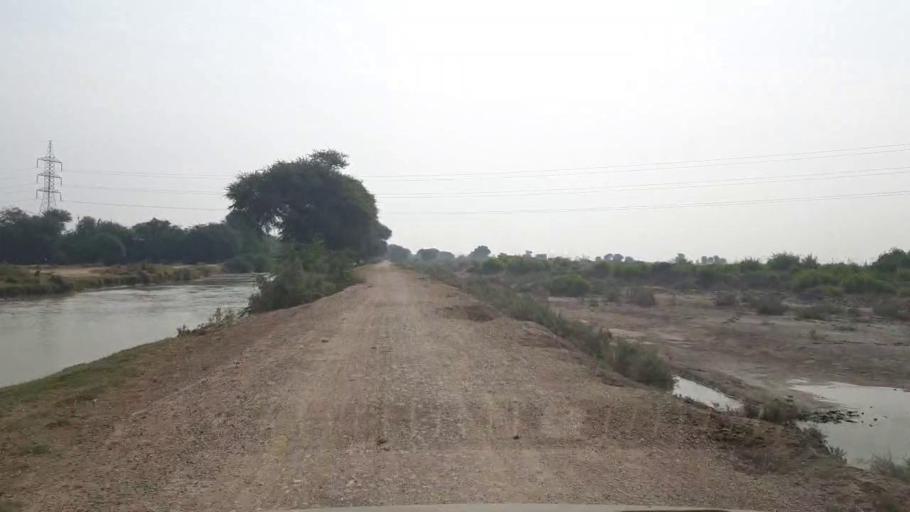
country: PK
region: Sindh
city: Tando Muhammad Khan
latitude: 25.1266
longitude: 68.4359
